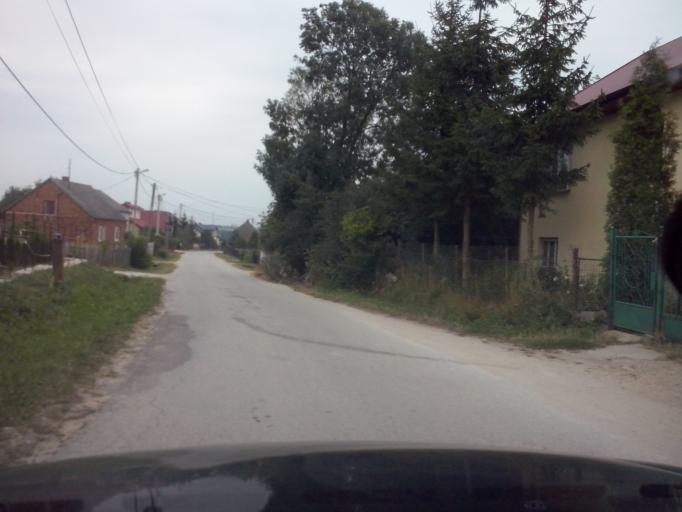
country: PL
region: Swietokrzyskie
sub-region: Powiat kielecki
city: Morawica
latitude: 50.6928
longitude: 20.5724
